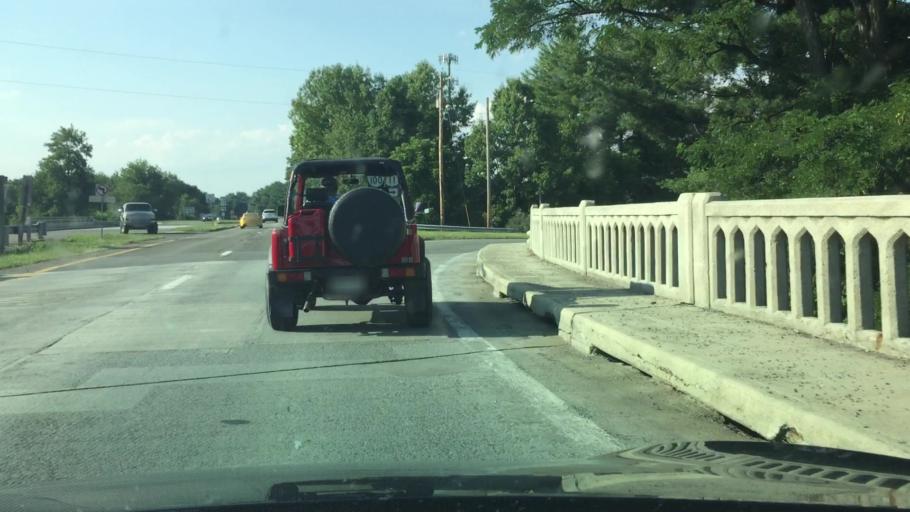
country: US
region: Virginia
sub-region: Pulaski County
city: Dublin
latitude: 37.1017
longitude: -80.6908
